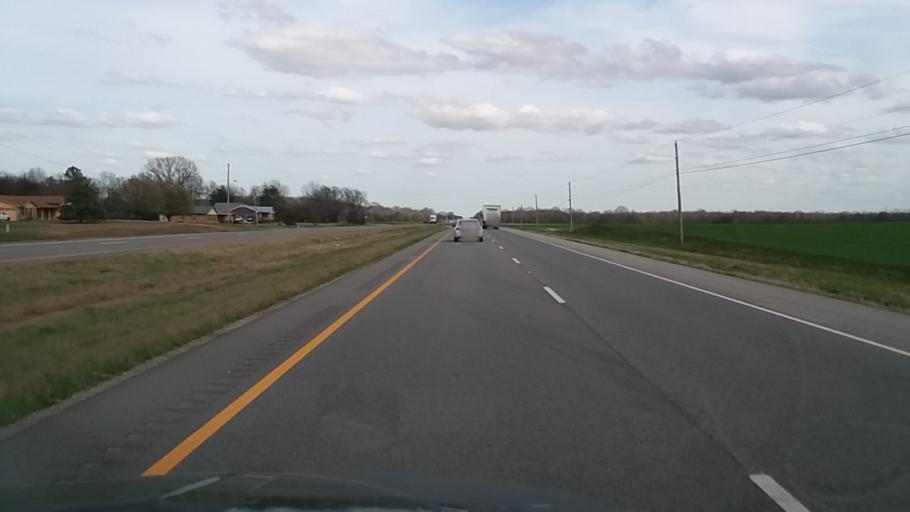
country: US
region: Alabama
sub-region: Colbert County
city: Muscle Shoals
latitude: 34.6845
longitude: -87.5588
